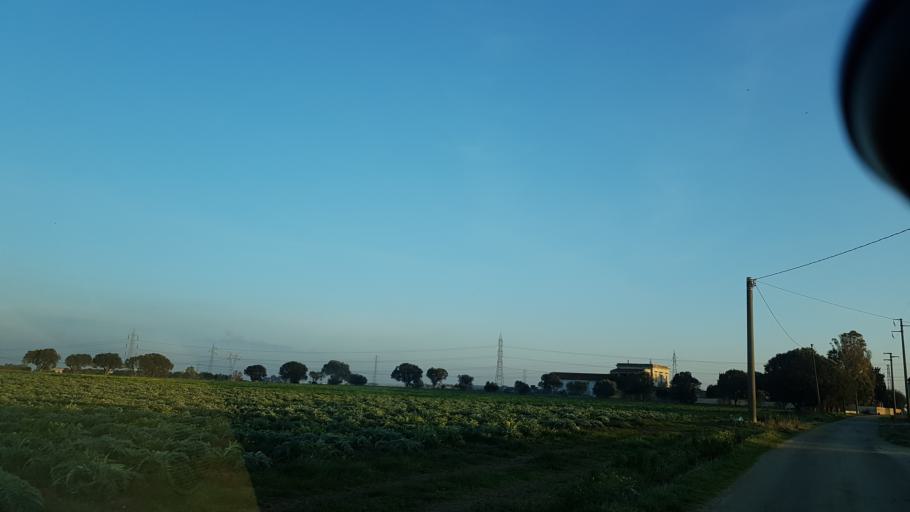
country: IT
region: Apulia
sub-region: Provincia di Brindisi
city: La Rosa
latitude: 40.6041
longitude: 17.9394
